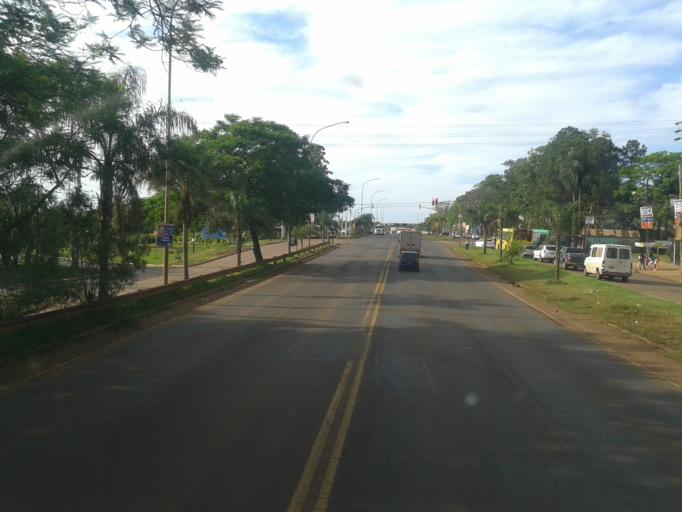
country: AR
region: Misiones
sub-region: Departamento de Capital
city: Posadas
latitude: -27.4128
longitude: -55.9014
